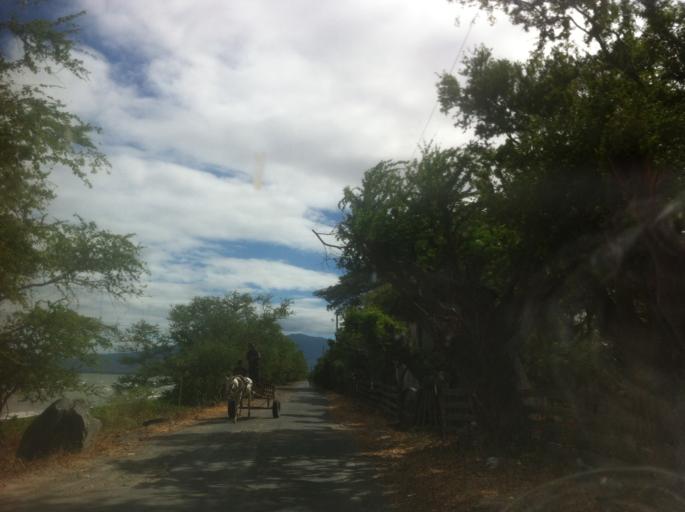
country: NI
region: Granada
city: Granada
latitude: 11.9825
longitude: -85.9405
